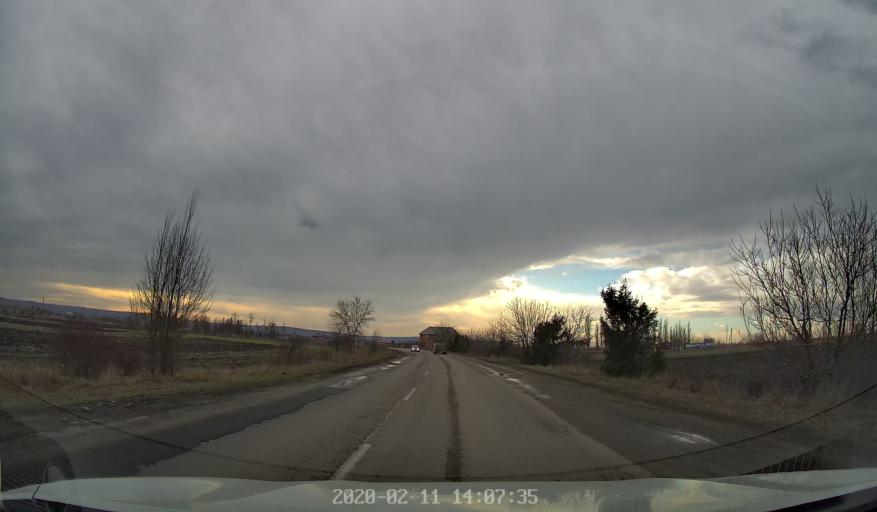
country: RO
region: Botosani
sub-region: Comuna Darabani
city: Bajura
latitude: 48.2457
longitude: 26.5518
